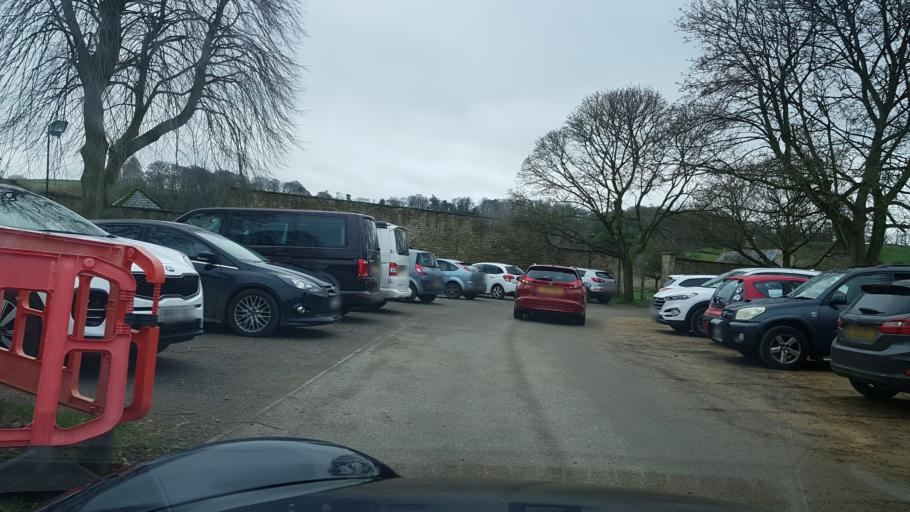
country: GB
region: England
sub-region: Somerset
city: Stoke-sub-Hamdon
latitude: 50.9509
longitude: -2.7146
